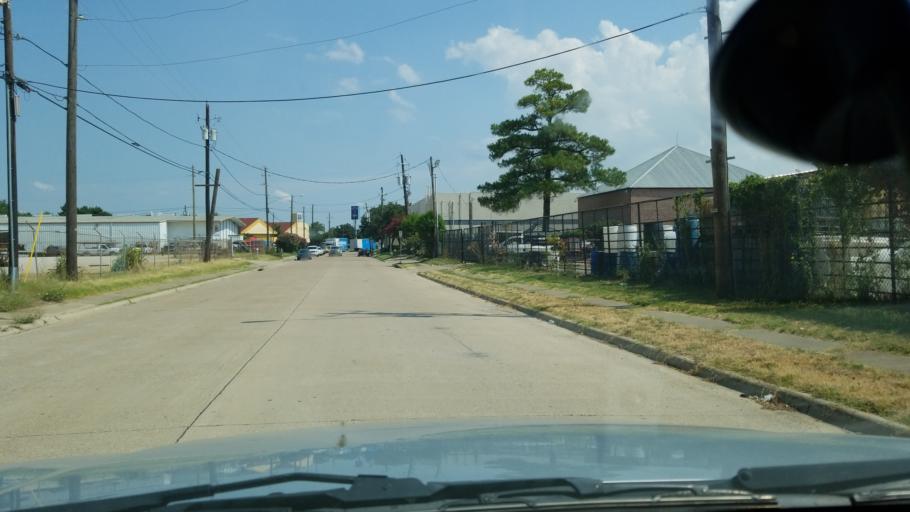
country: US
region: Texas
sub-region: Dallas County
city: Farmers Branch
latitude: 32.8621
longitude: -96.9030
